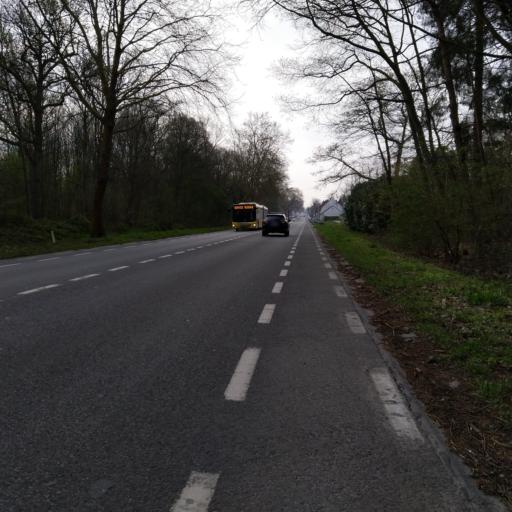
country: BE
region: Wallonia
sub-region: Province du Hainaut
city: Mons
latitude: 50.4940
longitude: 3.9386
